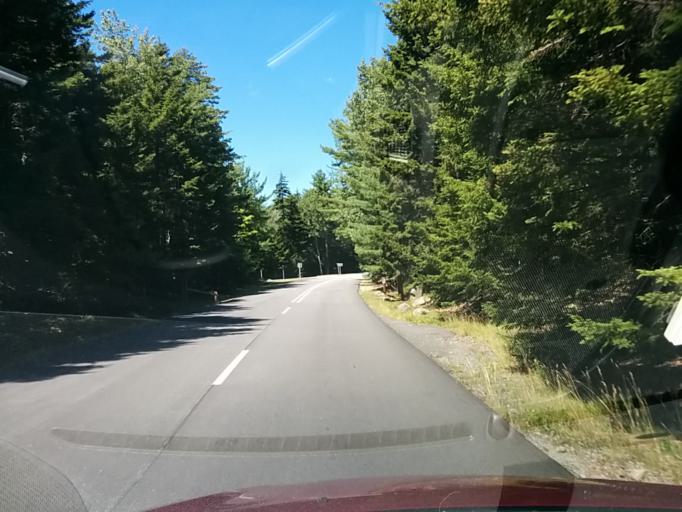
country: US
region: Maine
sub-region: Hancock County
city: Bar Harbor
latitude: 44.3129
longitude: -68.2458
